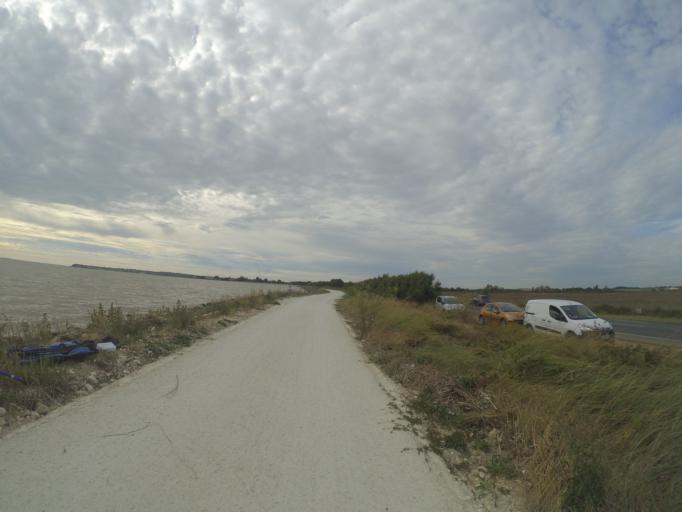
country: FR
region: Poitou-Charentes
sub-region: Departement de la Charente-Maritime
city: Meschers-sur-Gironde
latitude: 45.5473
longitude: -0.9128
